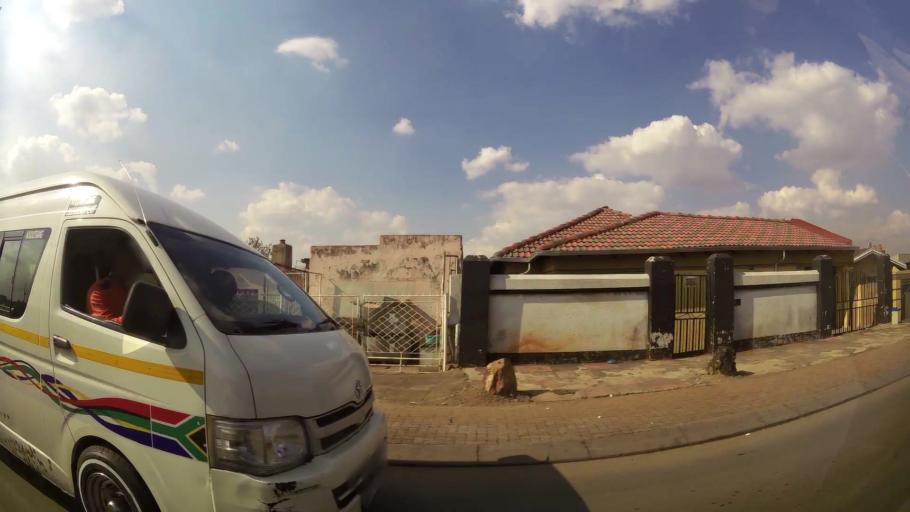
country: ZA
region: Gauteng
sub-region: Ekurhuleni Metropolitan Municipality
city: Germiston
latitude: -26.3164
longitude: 28.1576
